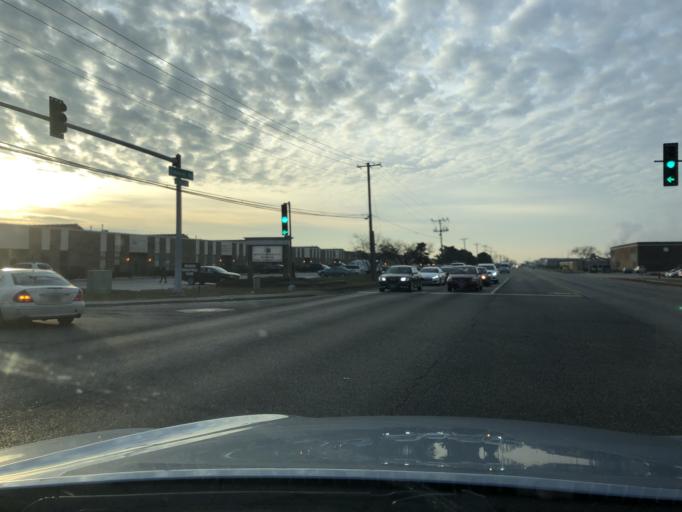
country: US
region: Illinois
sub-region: Cook County
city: Elk Grove Village
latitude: 42.0045
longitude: -87.9402
